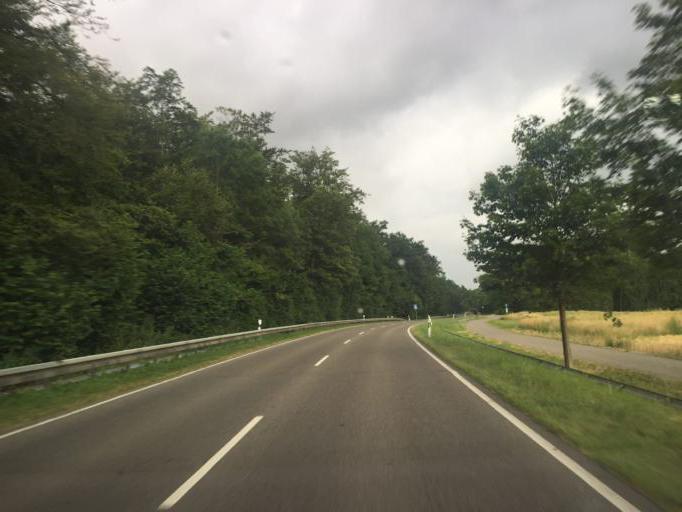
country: DE
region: Baden-Wuerttemberg
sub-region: Regierungsbezirk Stuttgart
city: Nufringen
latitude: 48.6463
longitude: 8.8627
